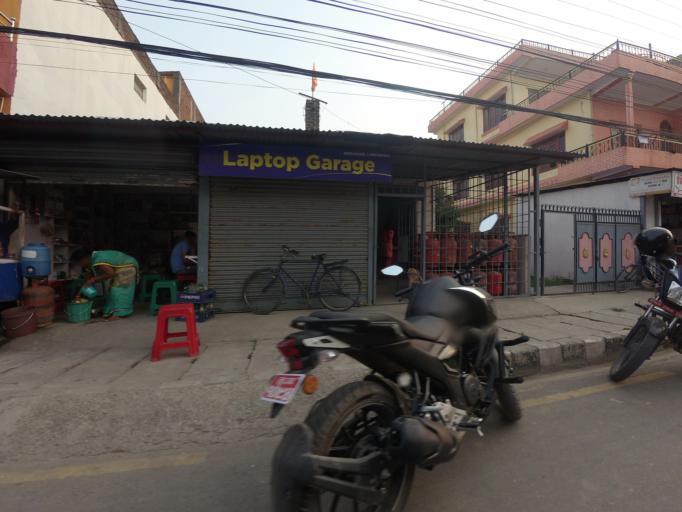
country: NP
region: Western Region
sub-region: Lumbini Zone
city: Bhairahawa
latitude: 27.5141
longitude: 83.4482
